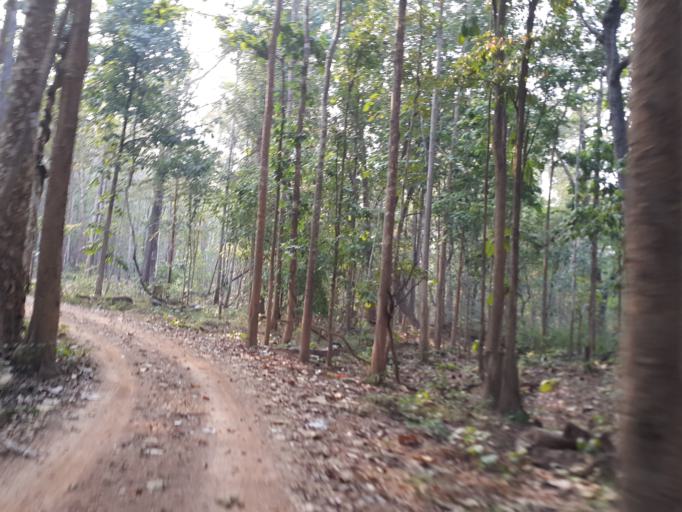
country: TH
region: Lamphun
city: Li
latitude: 17.6068
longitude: 98.9478
